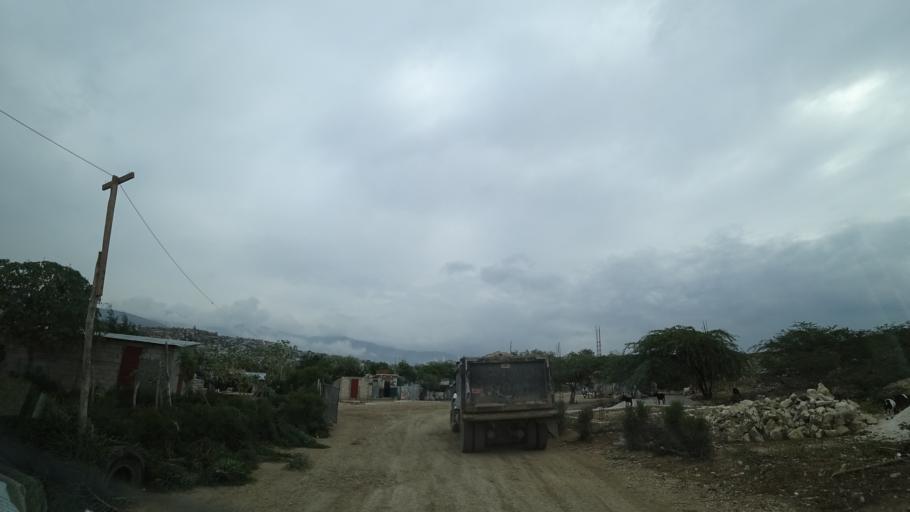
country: HT
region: Ouest
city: Croix des Bouquets
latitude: 18.6488
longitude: -72.2730
